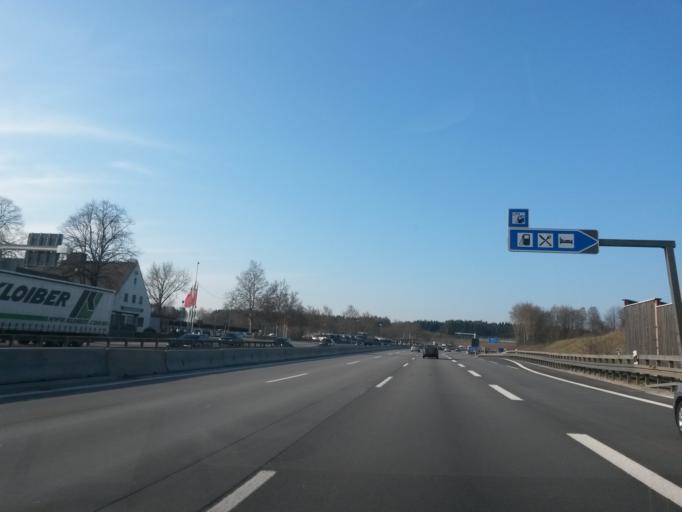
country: DE
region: Bavaria
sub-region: Upper Bavaria
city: Schweitenkirchen
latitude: 48.5533
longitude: 11.5903
